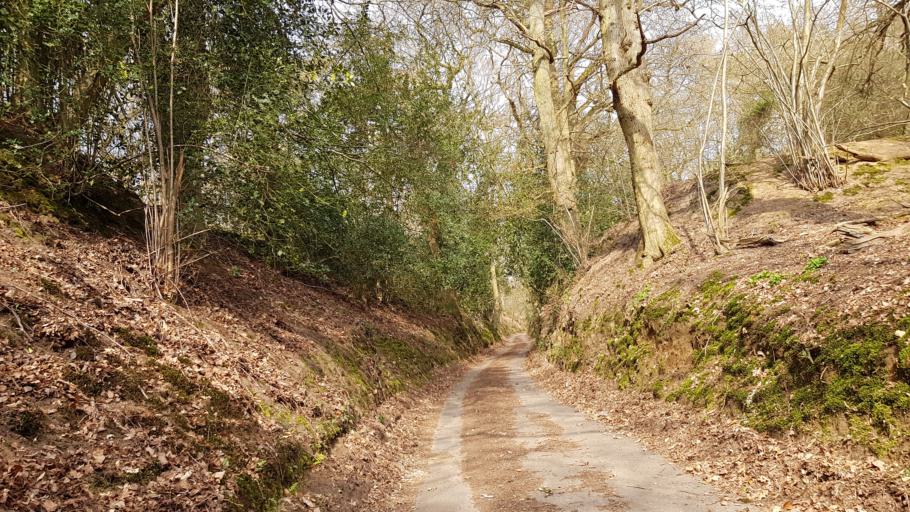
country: GB
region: England
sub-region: Surrey
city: Chilworth
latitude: 51.2093
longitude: -0.4892
